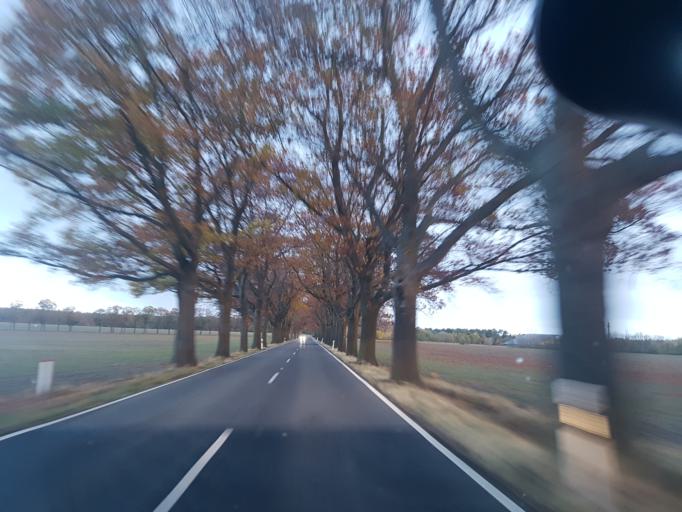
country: DE
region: Brandenburg
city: Ludwigsfelde
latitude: 52.2750
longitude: 13.2166
